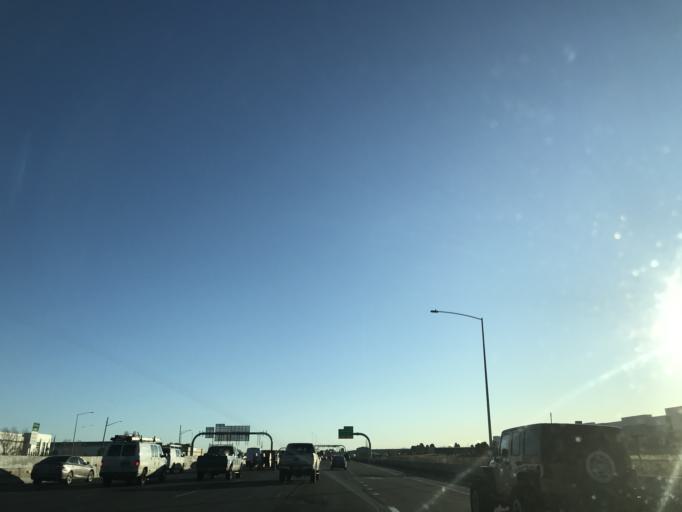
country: US
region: Colorado
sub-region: Adams County
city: Aurora
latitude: 39.7764
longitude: -104.8766
